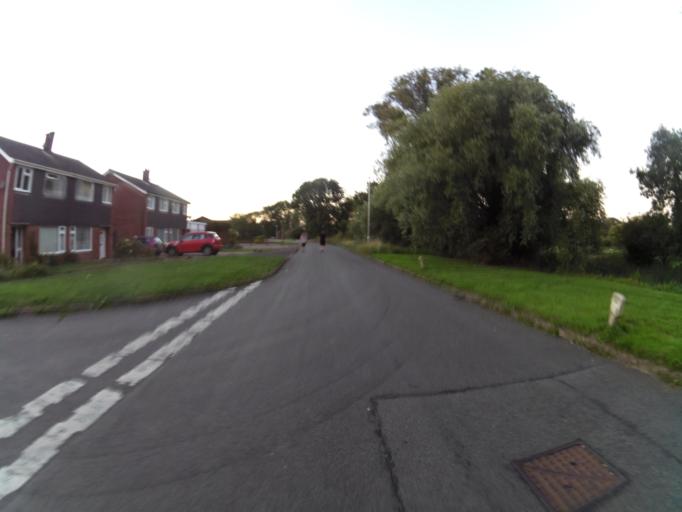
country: GB
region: England
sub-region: Suffolk
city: Bramford
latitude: 52.0792
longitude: 1.1015
